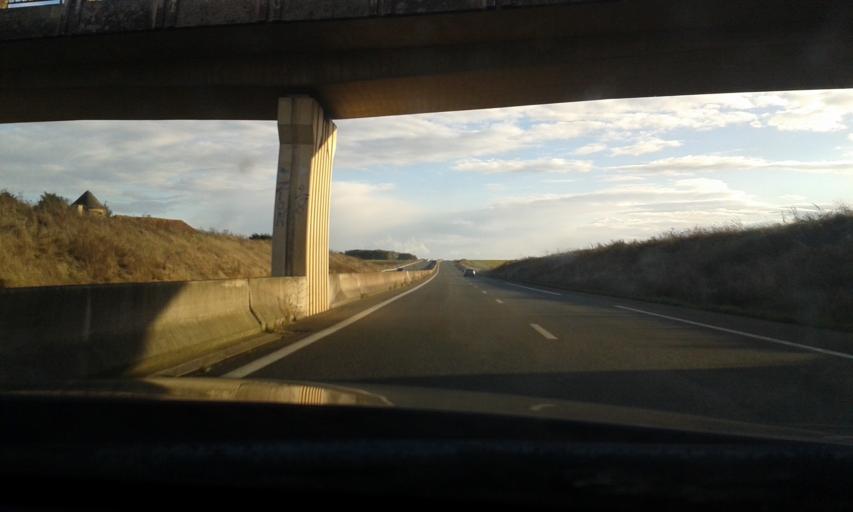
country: FR
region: Centre
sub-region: Departement d'Eure-et-Loir
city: Villemeux-sur-Eure
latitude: 48.5839
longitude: 1.4285
